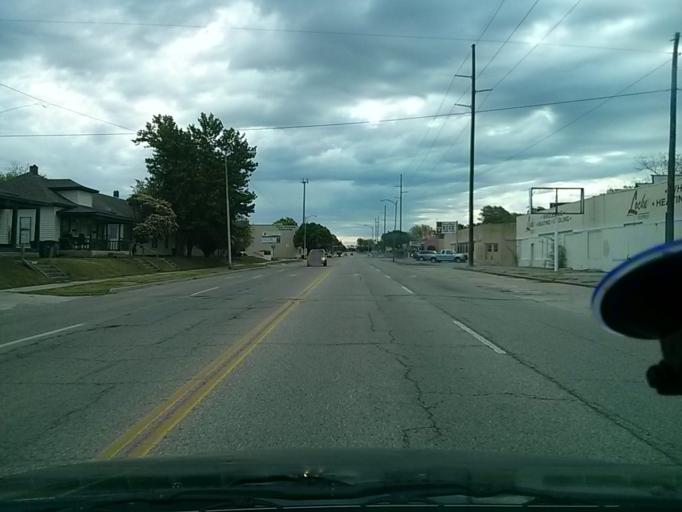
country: US
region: Oklahoma
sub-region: Tulsa County
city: Tulsa
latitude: 36.1566
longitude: -95.9630
